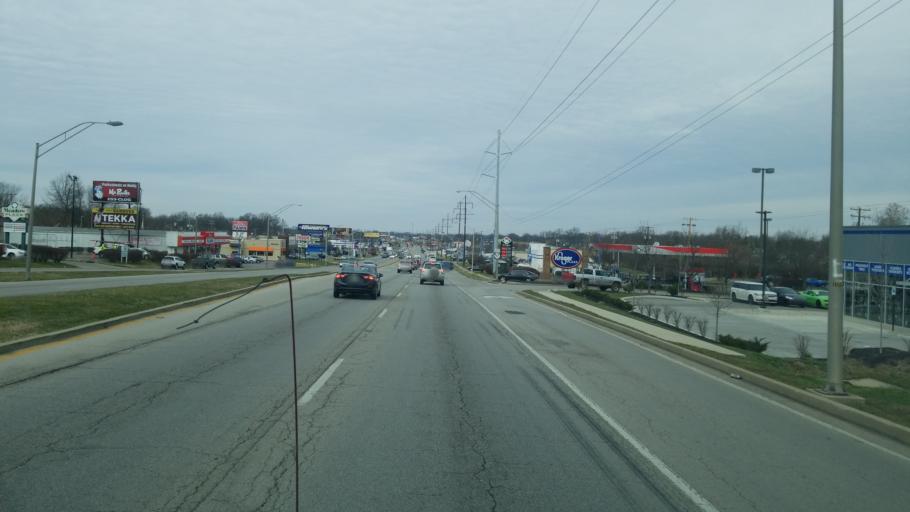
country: US
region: Kentucky
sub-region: Fayette County
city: Lexington-Fayette
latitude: 38.0583
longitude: -84.4631
